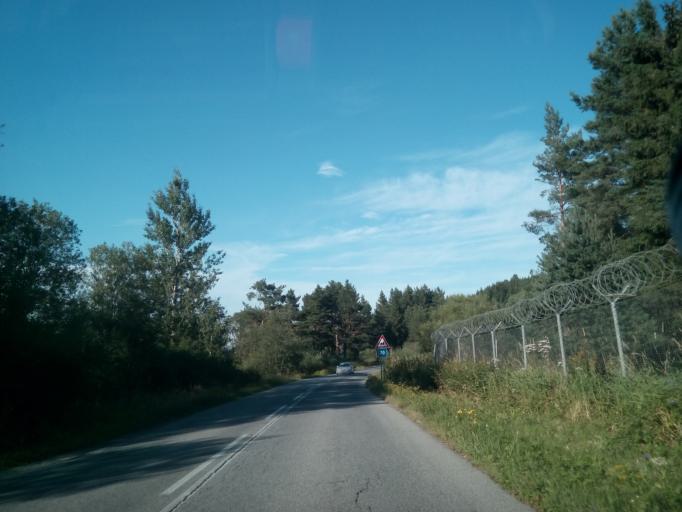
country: SK
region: Presovsky
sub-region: Okres Poprad
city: Poprad
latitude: 49.0246
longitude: 20.2532
